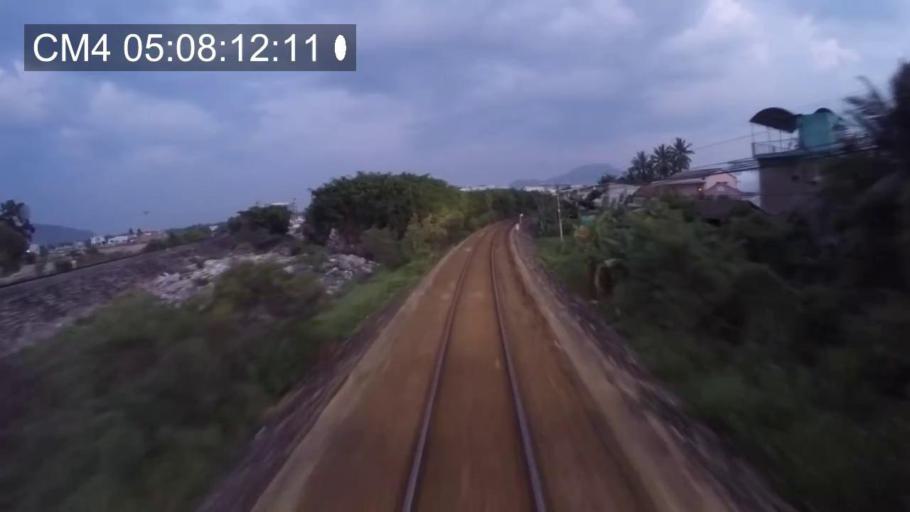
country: VN
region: Khanh Hoa
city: Nha Trang
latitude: 12.2908
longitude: 109.1861
